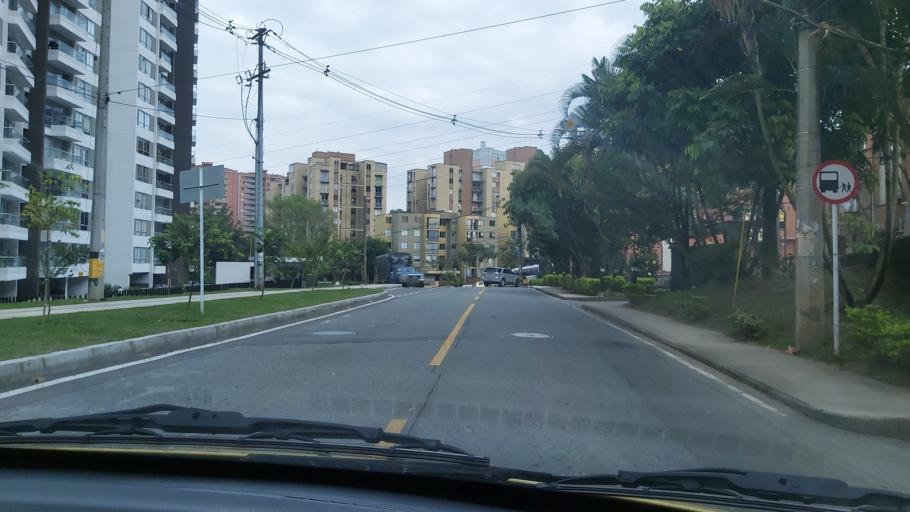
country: CO
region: Antioquia
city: Medellin
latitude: 6.2253
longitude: -75.5611
